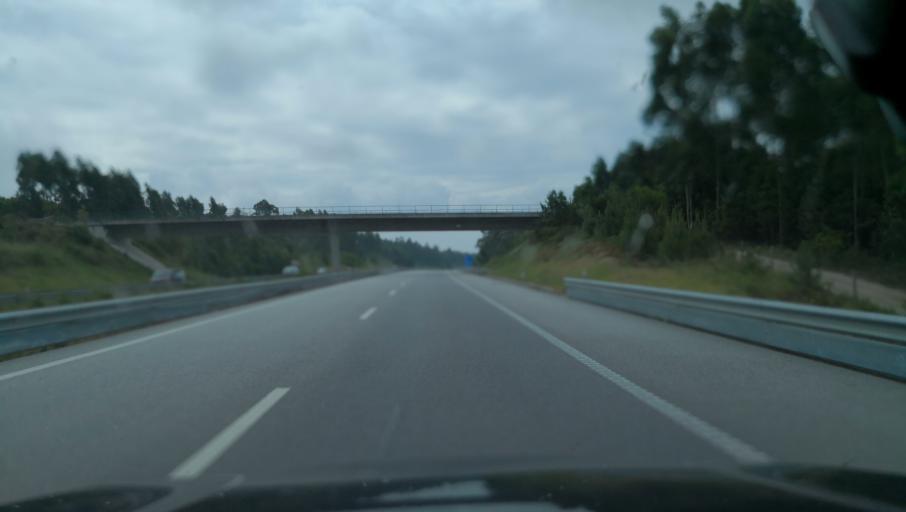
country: PT
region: Coimbra
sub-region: Figueira da Foz
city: Alhadas
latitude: 40.1714
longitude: -8.7910
